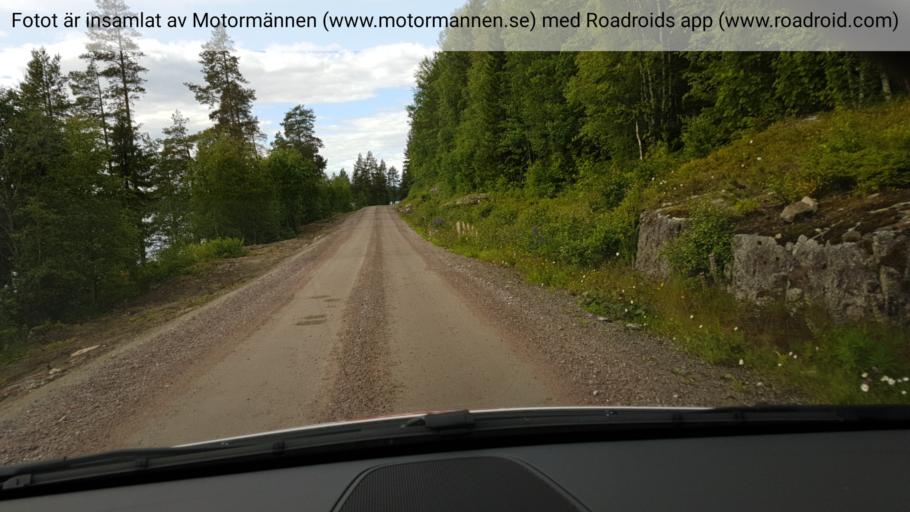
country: SE
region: Jaemtland
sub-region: Stroemsunds Kommun
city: Stroemsund
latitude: 63.9970
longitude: 15.9739
